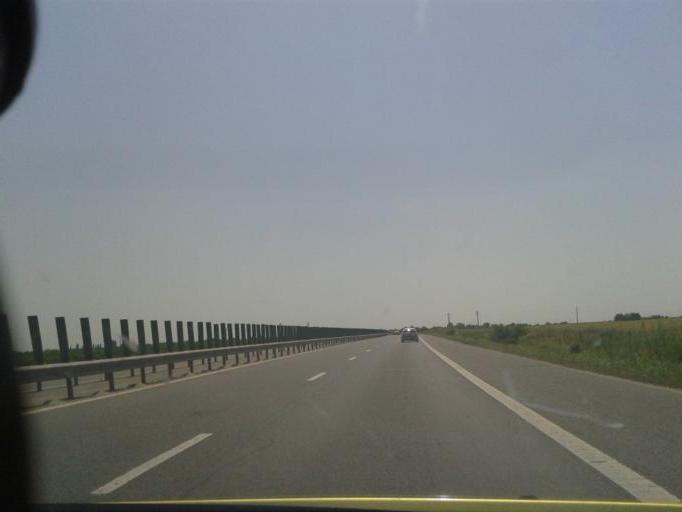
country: RO
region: Calarasi
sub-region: Comuna Sarulesti
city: Sarulesti-Gara
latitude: 44.4451
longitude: 26.6359
